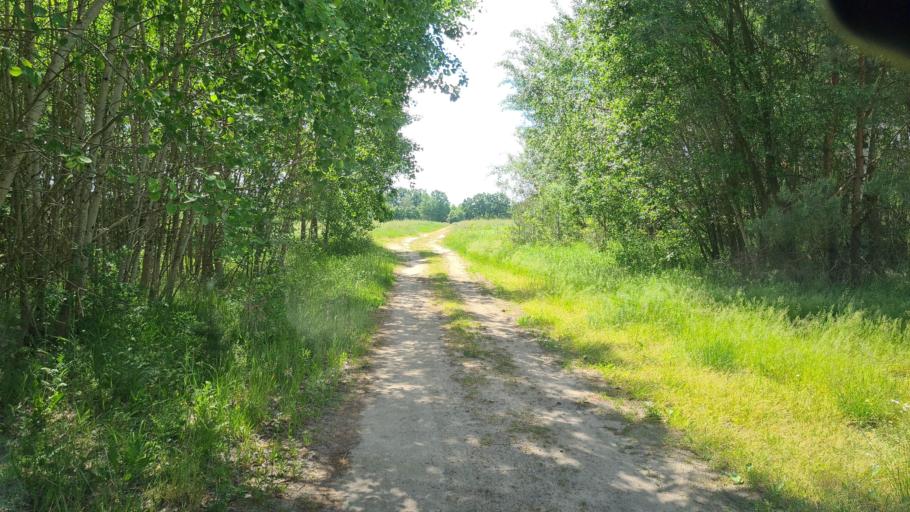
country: DE
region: Brandenburg
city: Sallgast
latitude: 51.5959
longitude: 13.8159
